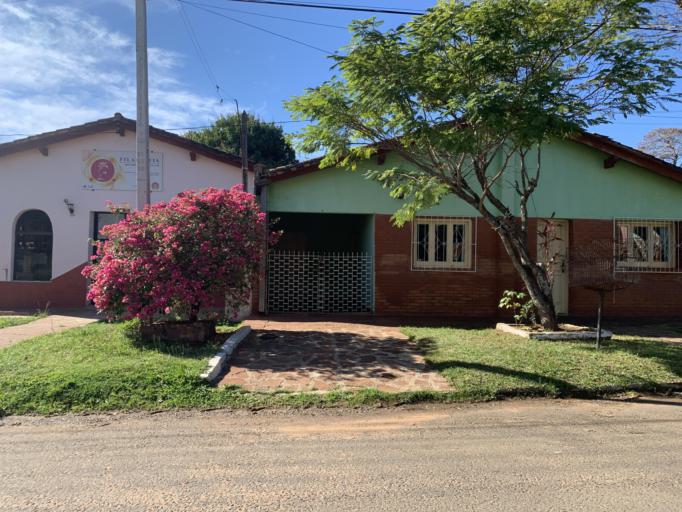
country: PY
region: Misiones
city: San Juan Bautista
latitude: -26.6691
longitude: -57.1376
